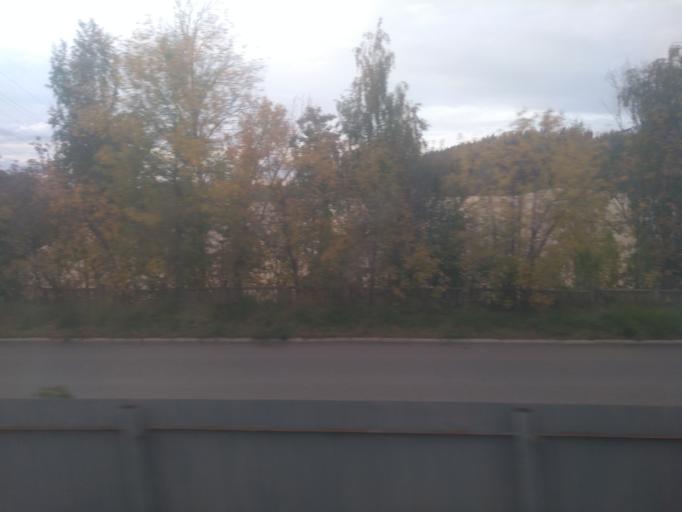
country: RU
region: Tatarstan
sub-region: Gorod Kazan'
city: Kazan
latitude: 55.8059
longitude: 49.0544
